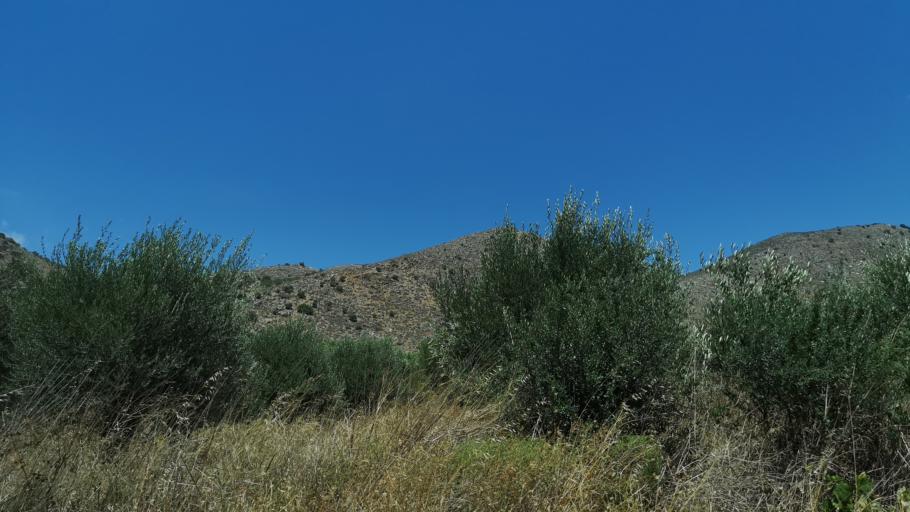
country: GR
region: Crete
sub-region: Nomos Lasithiou
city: Neapoli
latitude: 35.2469
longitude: 25.6300
